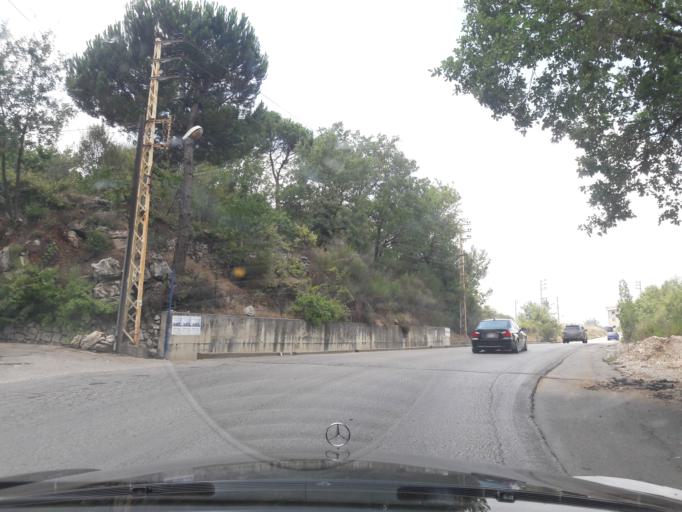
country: LB
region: Mont-Liban
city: Djounie
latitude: 33.9163
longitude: 35.6880
